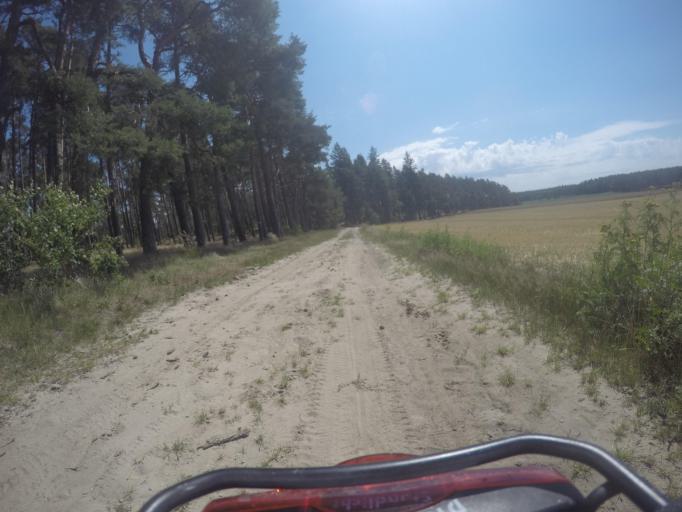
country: DE
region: Lower Saxony
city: Dahlem
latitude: 53.2262
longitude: 10.7240
